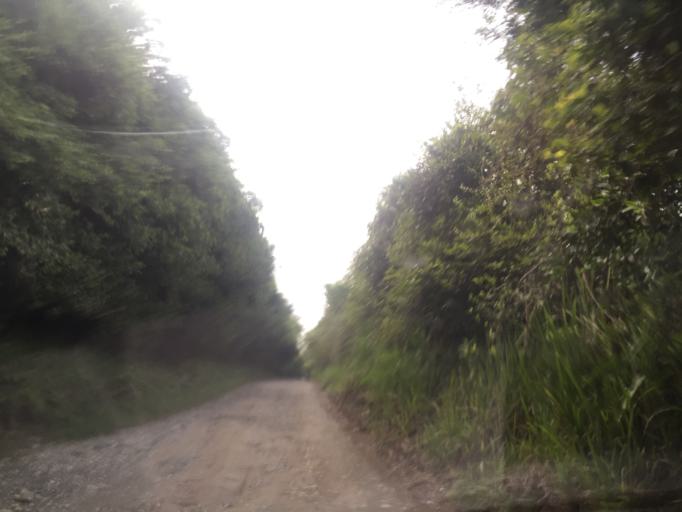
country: CO
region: Quindio
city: La Tebaida
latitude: 4.4679
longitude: -75.8351
